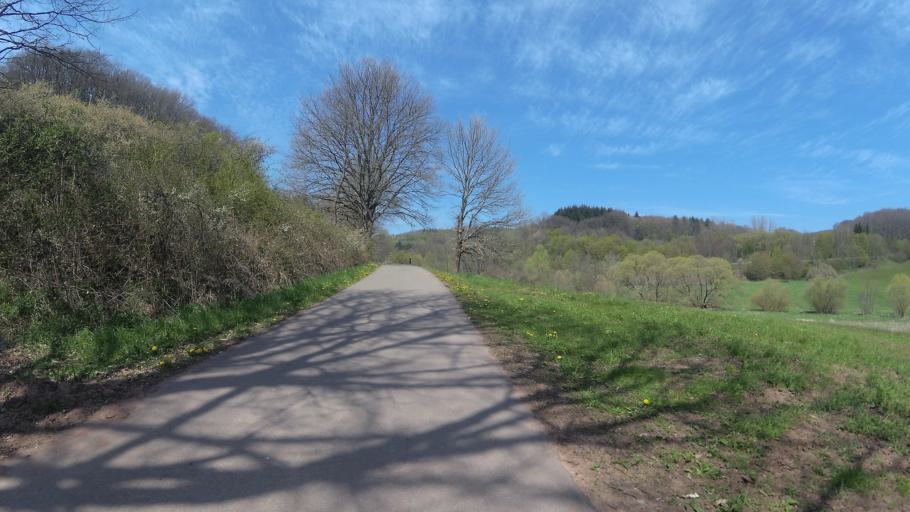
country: DE
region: Rheinland-Pfalz
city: Brucken
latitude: 49.4263
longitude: 7.3767
